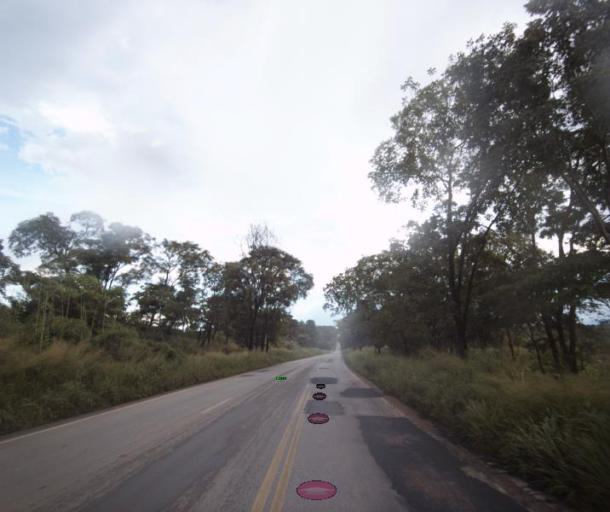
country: BR
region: Goias
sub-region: Porangatu
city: Porangatu
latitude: -13.9281
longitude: -49.0716
